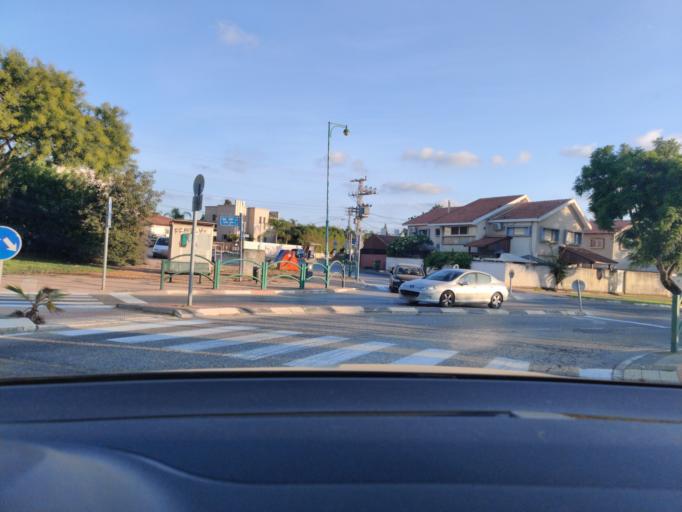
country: IL
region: Central District
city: Elyakhin
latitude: 32.4323
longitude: 34.9426
